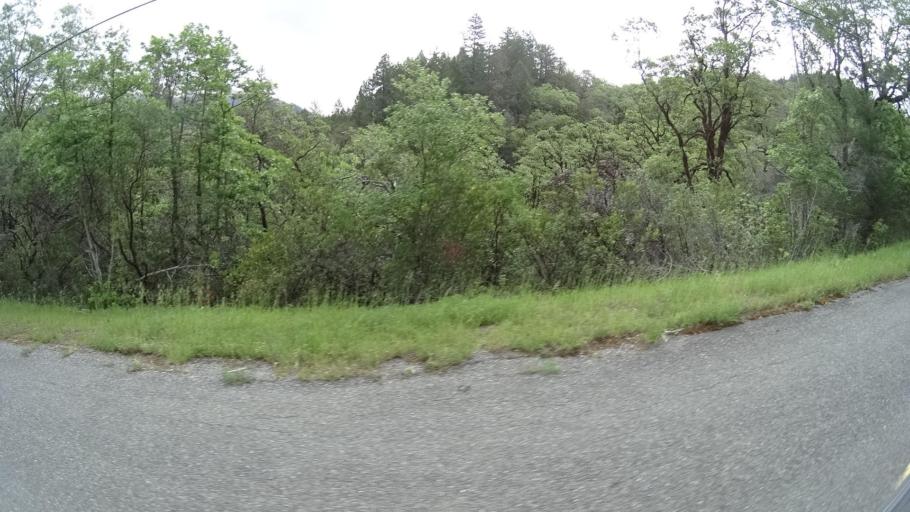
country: US
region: California
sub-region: Humboldt County
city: Redway
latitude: 40.1882
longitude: -123.5875
